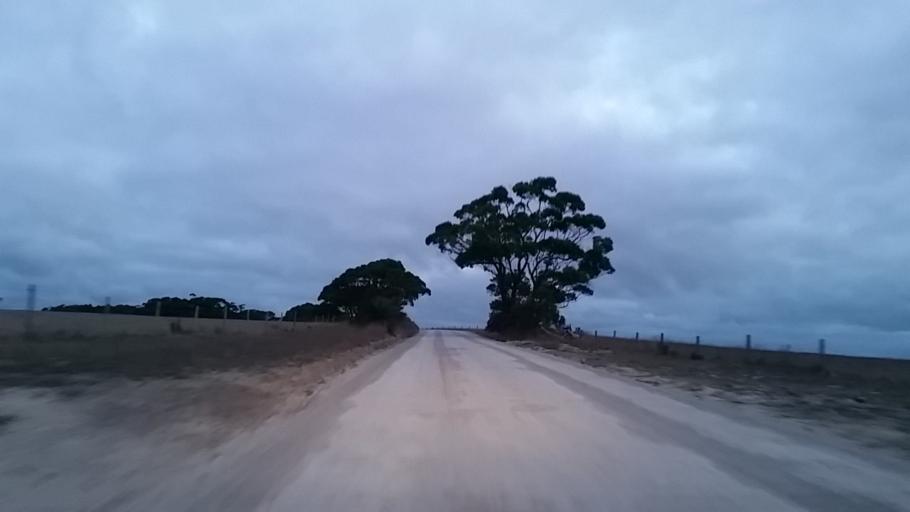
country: AU
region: South Australia
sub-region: Yankalilla
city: Normanville
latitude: -35.6094
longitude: 138.1997
